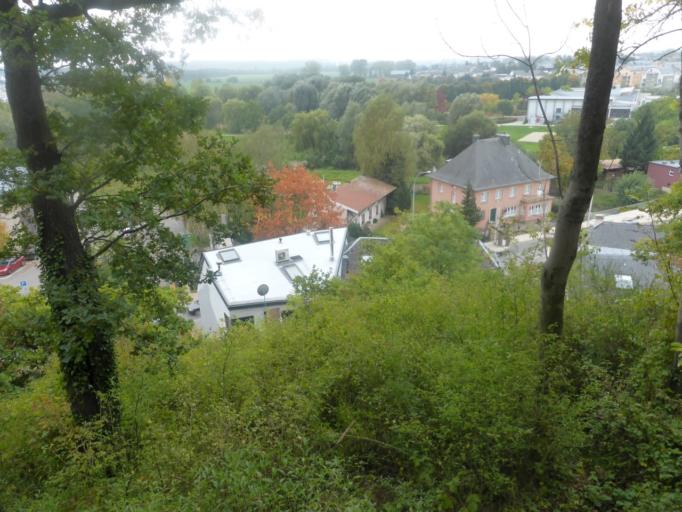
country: LU
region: Luxembourg
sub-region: Canton de Luxembourg
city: Hesperange
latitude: 49.5738
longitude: 6.1572
